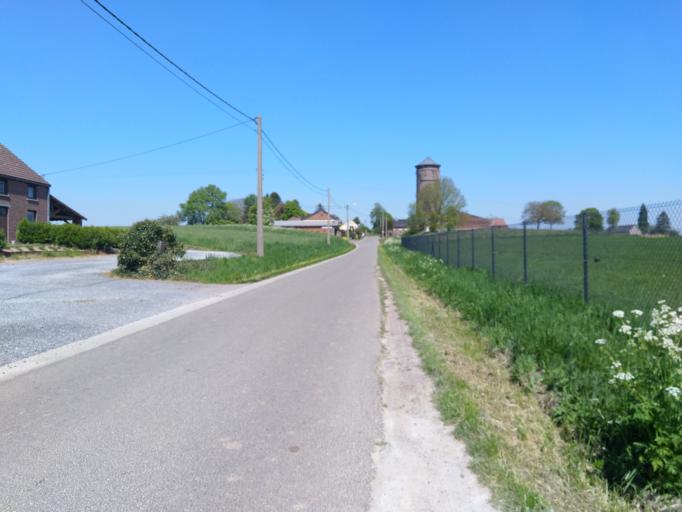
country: BE
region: Wallonia
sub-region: Province du Hainaut
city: Enghien
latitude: 50.6293
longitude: 4.0179
